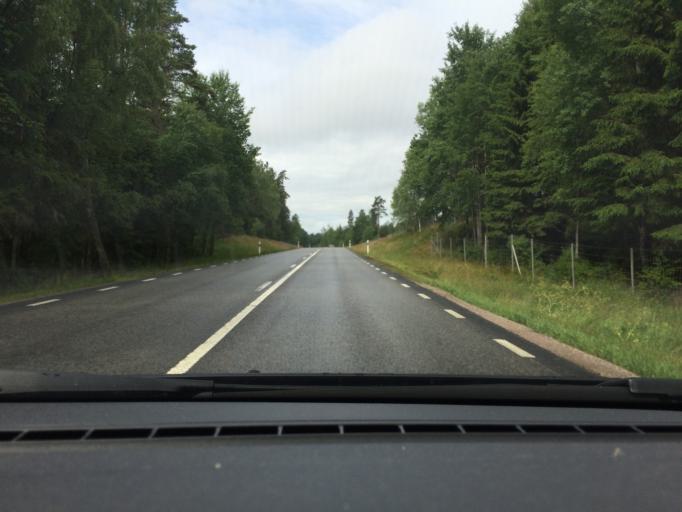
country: SE
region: Joenkoeping
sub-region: Varnamo Kommun
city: Forsheda
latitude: 57.1625
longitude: 13.8659
